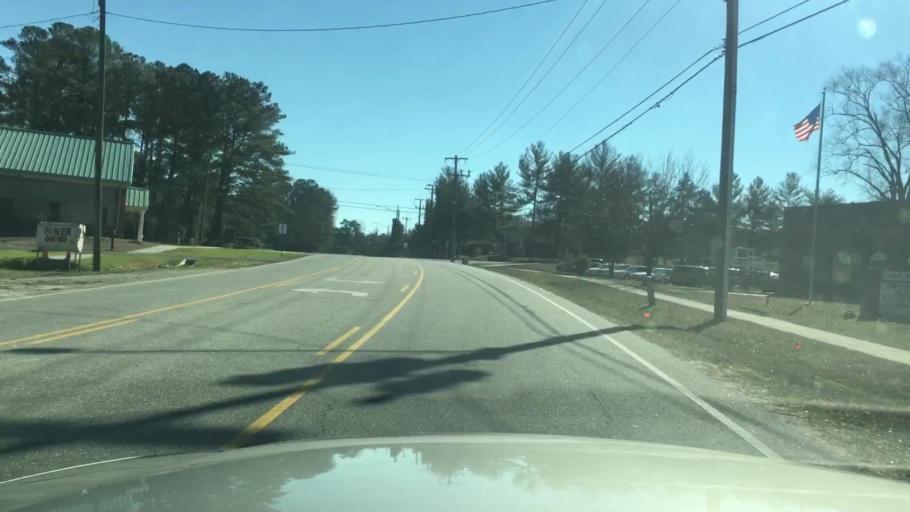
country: US
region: North Carolina
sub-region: Cumberland County
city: Fayetteville
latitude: 35.0370
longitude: -78.8951
